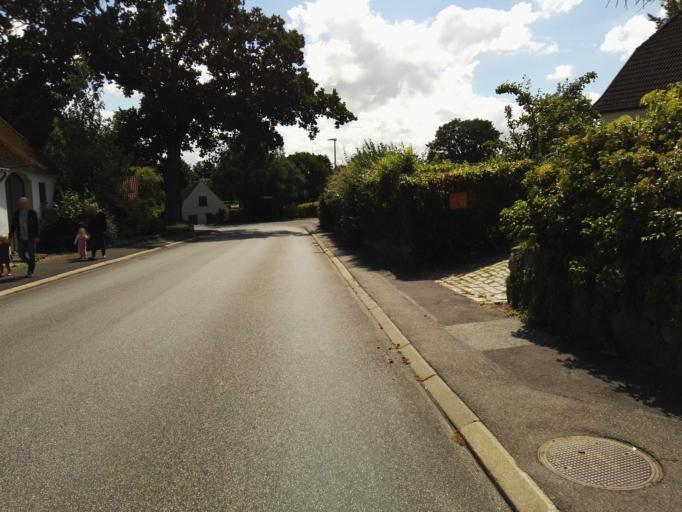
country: DK
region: Capital Region
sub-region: Egedal Kommune
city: Stenlose
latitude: 55.8009
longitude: 12.2217
